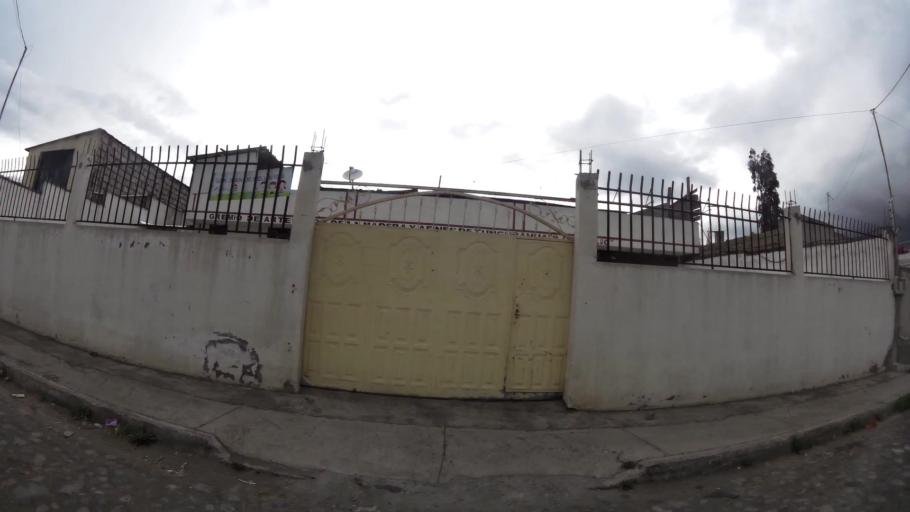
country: EC
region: Tungurahua
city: Ambato
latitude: -1.2680
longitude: -78.6185
